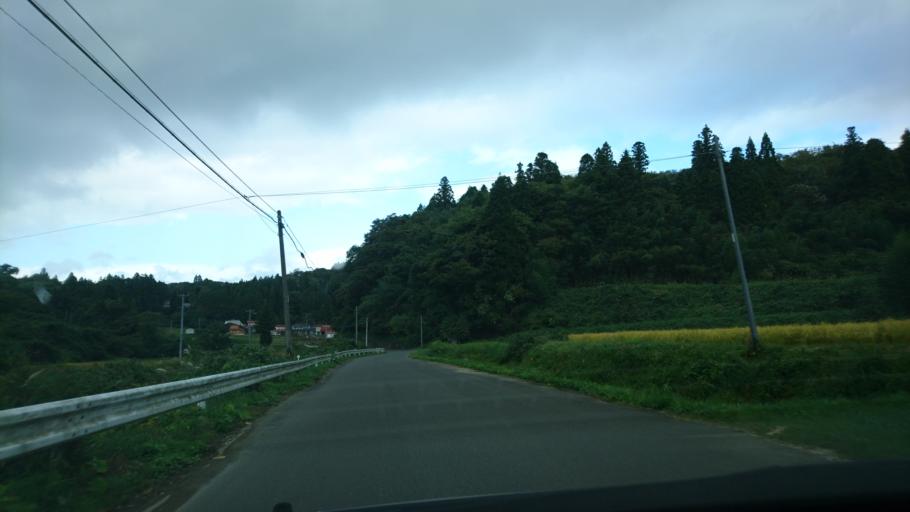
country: JP
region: Iwate
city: Ichinoseki
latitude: 38.9085
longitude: 141.0803
